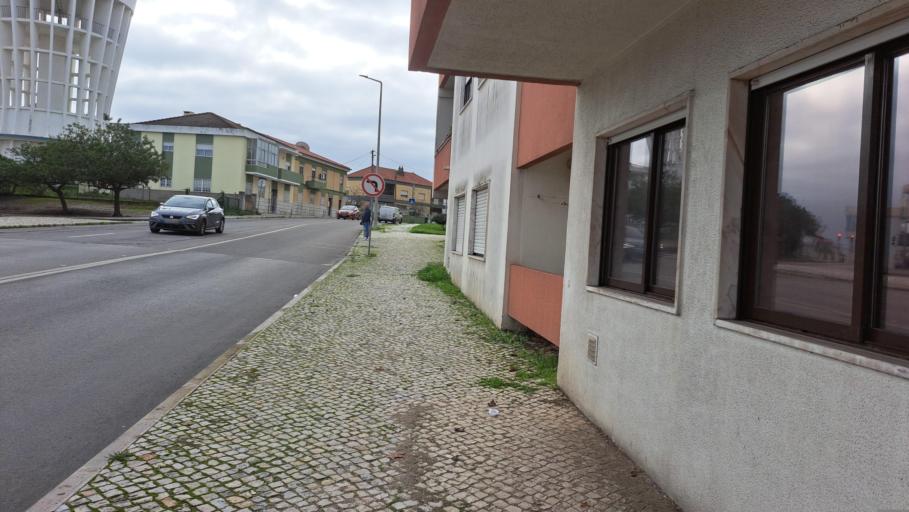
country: PT
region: Setubal
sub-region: Moita
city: Alhos Vedros
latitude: 38.6541
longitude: -9.0472
